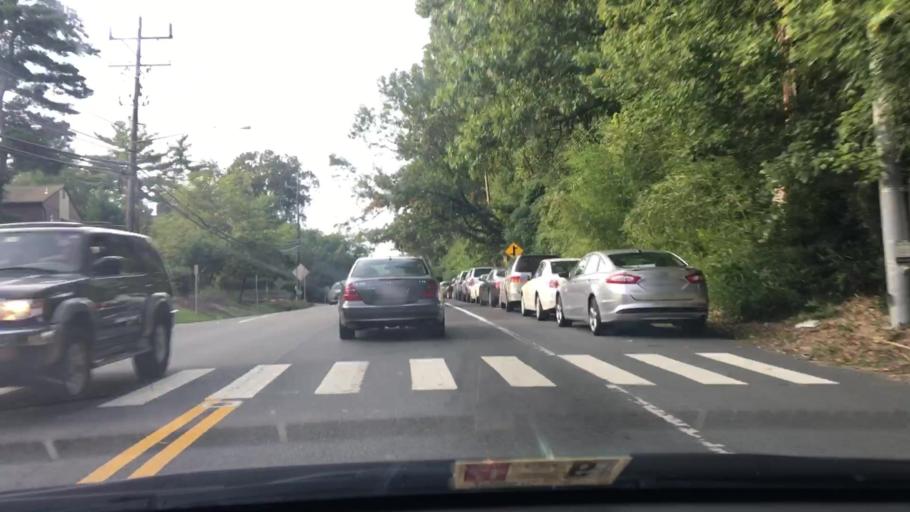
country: US
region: Maryland
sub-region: Montgomery County
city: North Bethesda
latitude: 39.0313
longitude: -77.1616
